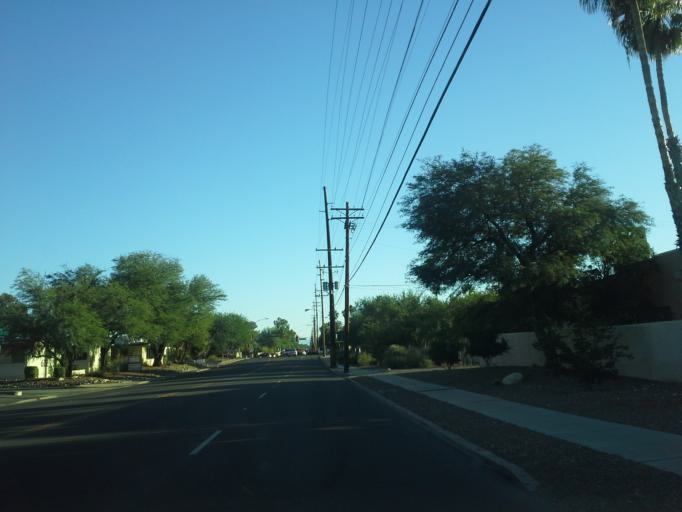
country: US
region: Arizona
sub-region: Pima County
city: Tucson
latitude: 32.2305
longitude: -110.9268
